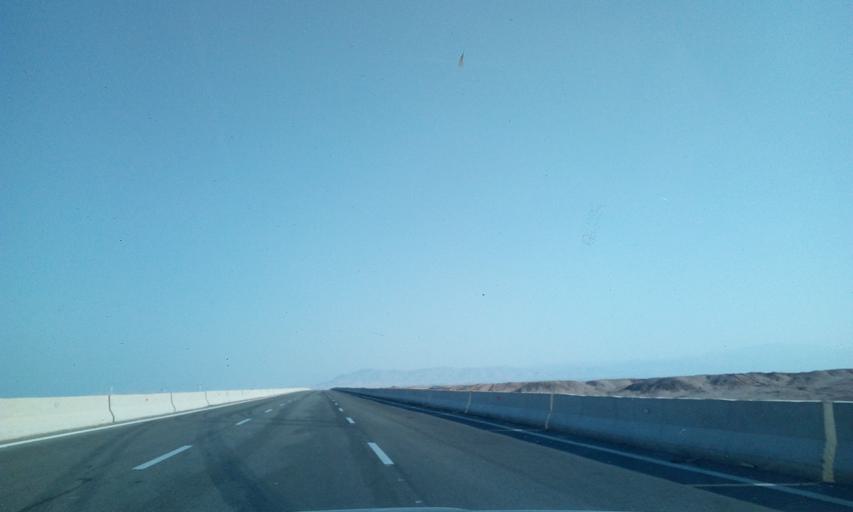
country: EG
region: As Suways
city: Ain Sukhna
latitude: 29.1817
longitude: 32.5023
